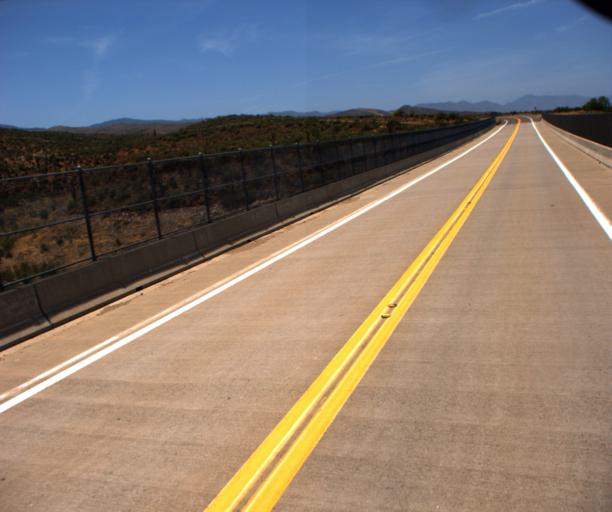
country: US
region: Arizona
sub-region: Gila County
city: Tonto Basin
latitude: 33.6959
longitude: -111.1812
